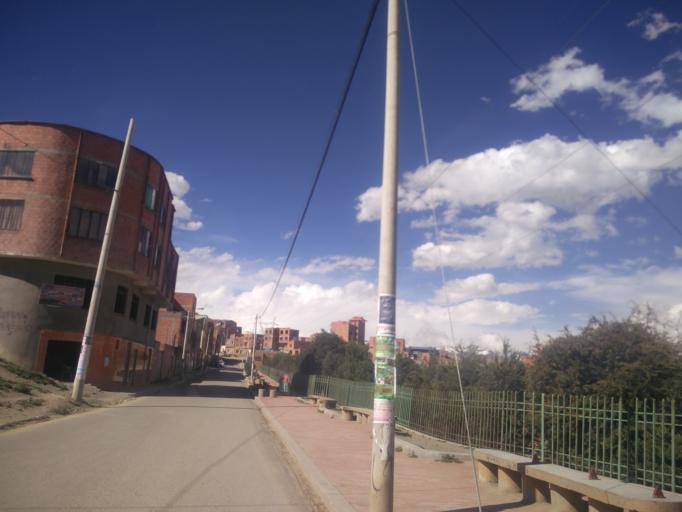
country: BO
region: La Paz
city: La Paz
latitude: -16.4825
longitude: -68.1683
